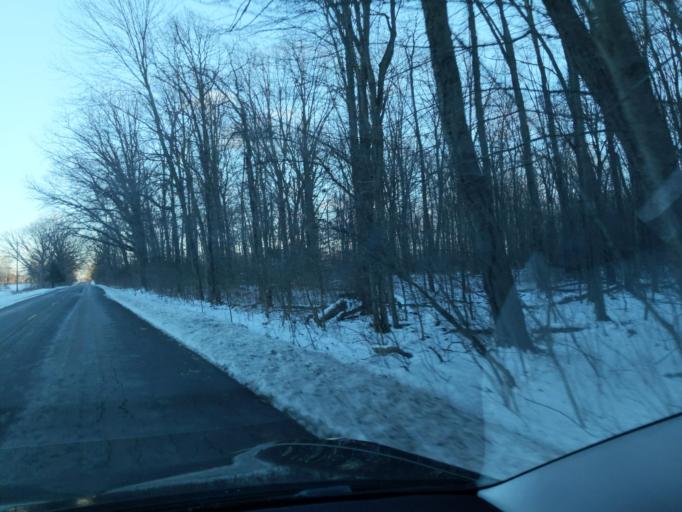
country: US
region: Michigan
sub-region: Ingham County
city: Stockbridge
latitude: 42.4612
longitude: -84.2370
